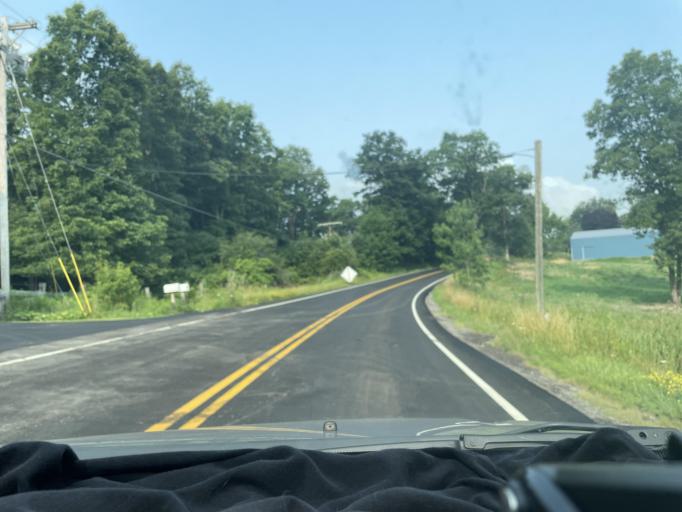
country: US
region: Maryland
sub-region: Garrett County
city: Mountain Lake Park
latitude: 39.2931
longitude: -79.3654
